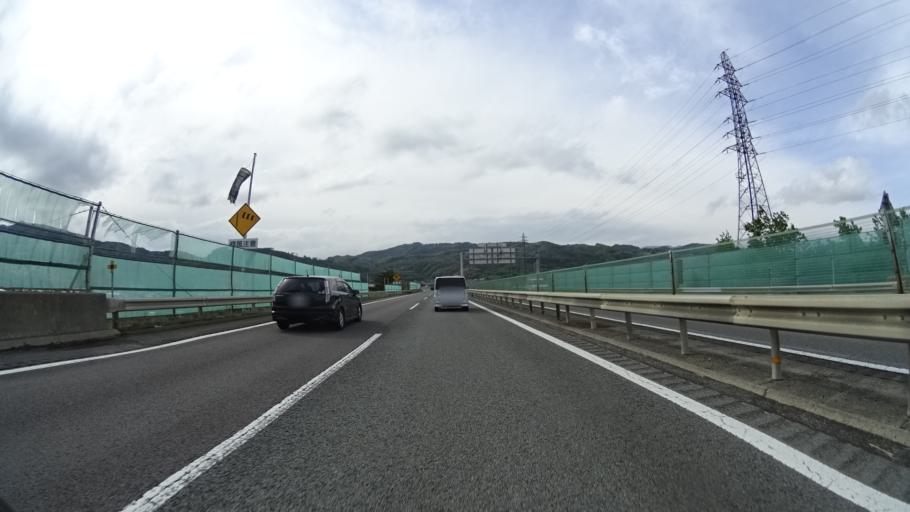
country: JP
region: Nagano
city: Nagano-shi
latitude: 36.5555
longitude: 138.1232
